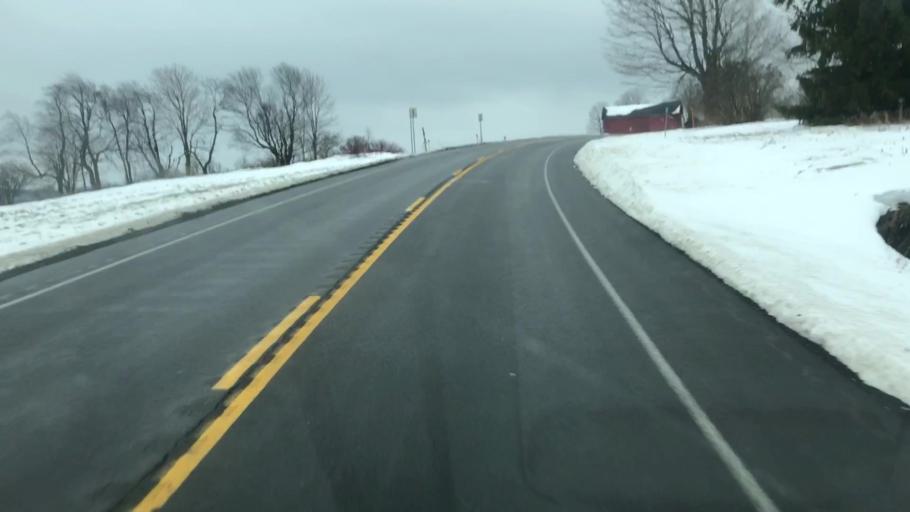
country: US
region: New York
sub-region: Cayuga County
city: Moravia
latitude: 42.7698
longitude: -76.3325
